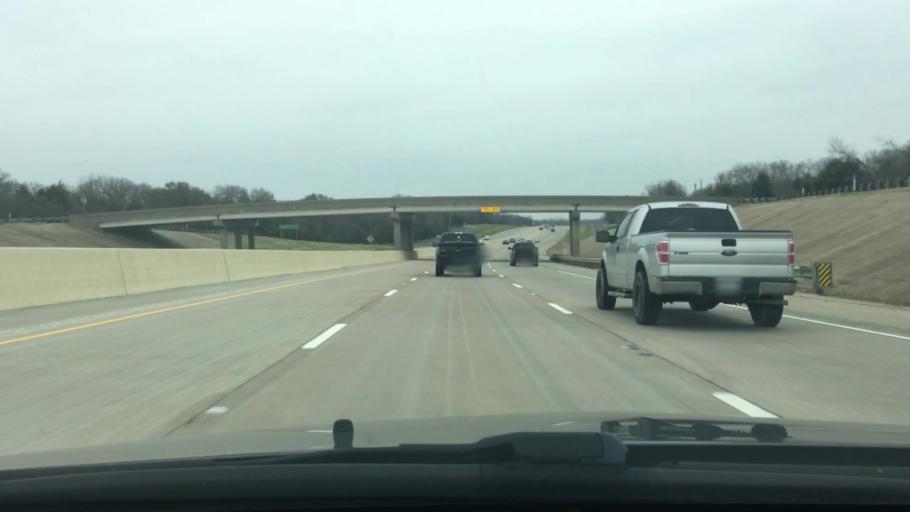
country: US
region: Texas
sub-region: Navarro County
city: Corsicana
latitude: 31.9642
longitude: -96.4207
